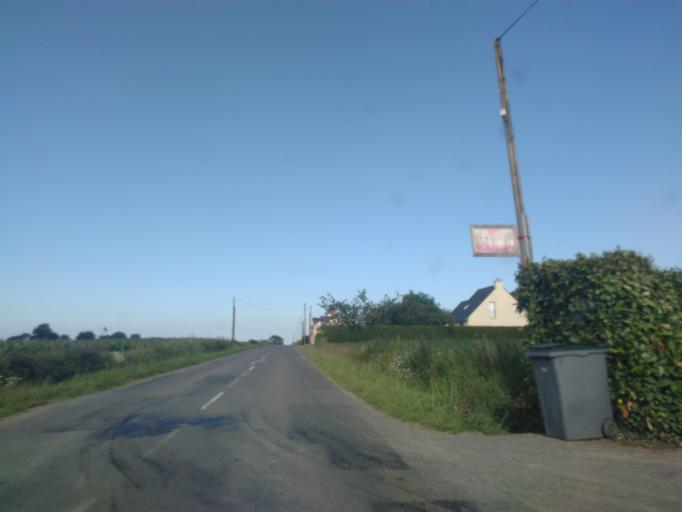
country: FR
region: Brittany
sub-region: Departement d'Ille-et-Vilaine
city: Romille
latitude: 48.2166
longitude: -1.8674
